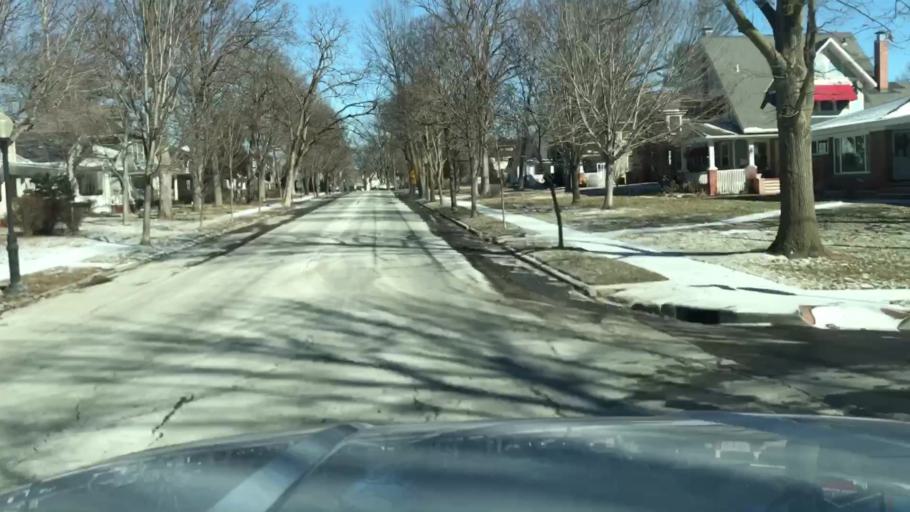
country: US
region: Missouri
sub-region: Buchanan County
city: Saint Joseph
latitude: 39.7825
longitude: -94.8239
